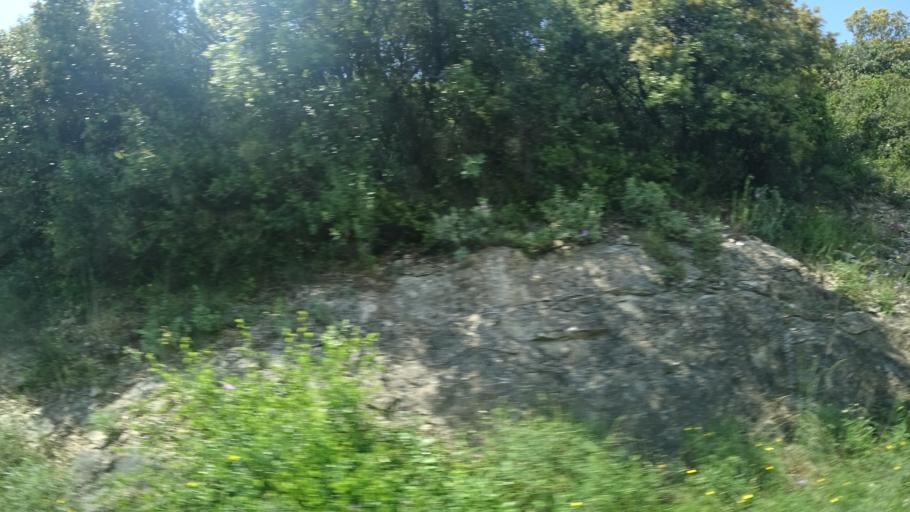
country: FR
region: Languedoc-Roussillon
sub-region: Departement de l'Herault
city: Olonzac
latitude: 43.3501
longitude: 2.7476
